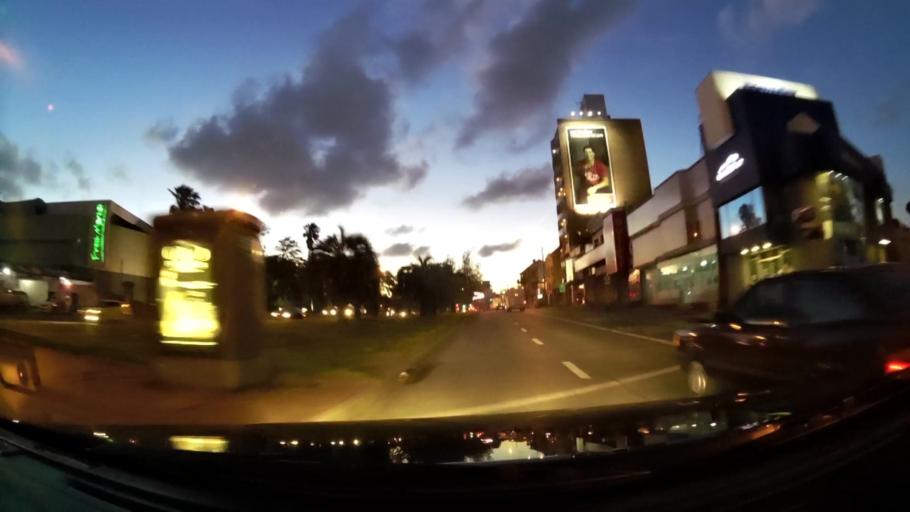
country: UY
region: Montevideo
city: Montevideo
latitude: -34.8866
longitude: -56.1402
